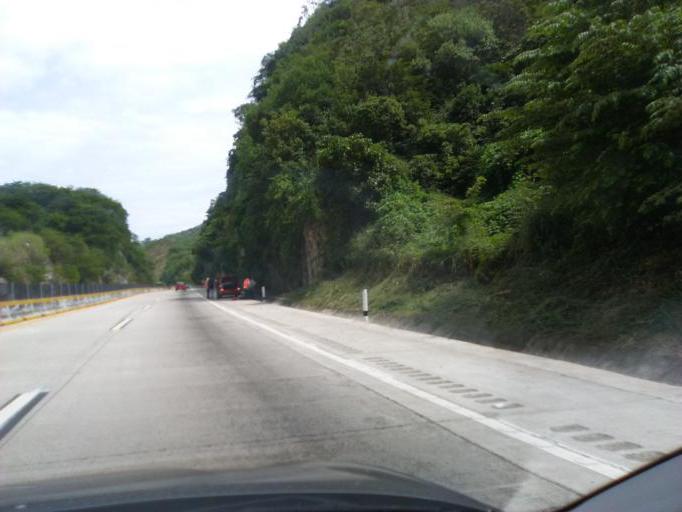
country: MX
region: Guerrero
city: Tierra Colorada
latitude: 17.1874
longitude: -99.5479
